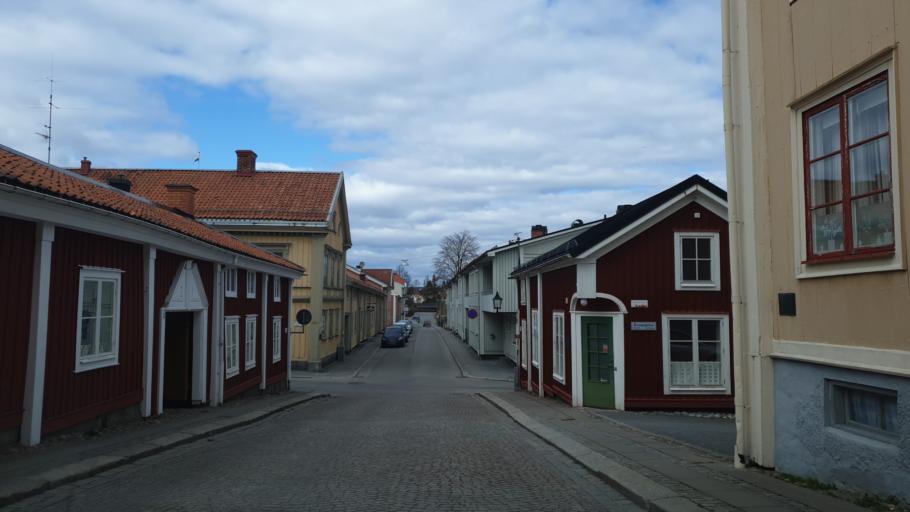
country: SE
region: OErebro
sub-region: Nora Kommun
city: Nora
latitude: 59.5205
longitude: 15.0415
